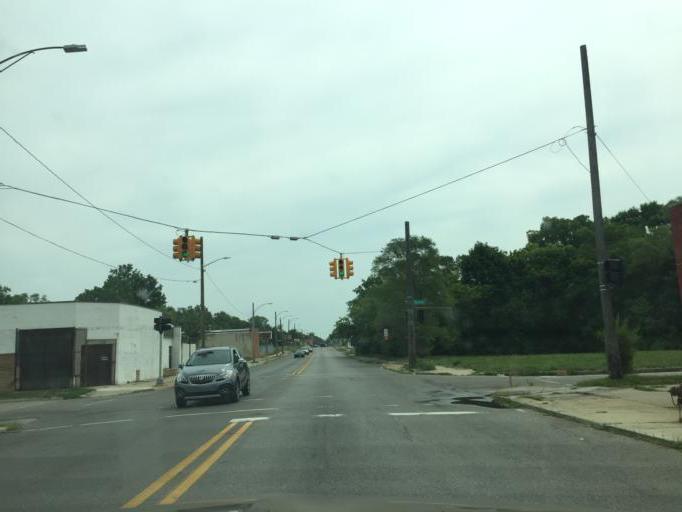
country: US
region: Michigan
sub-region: Wayne County
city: Redford
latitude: 42.4004
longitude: -83.2524
